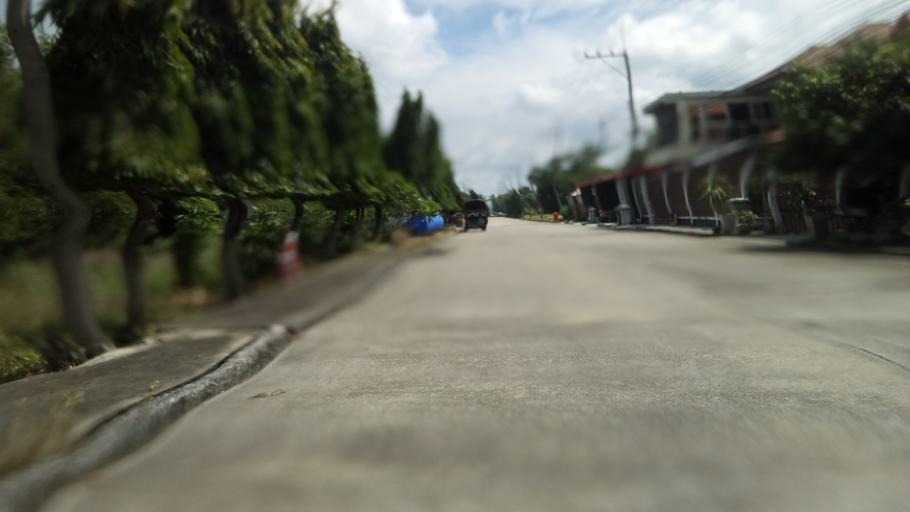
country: TH
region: Pathum Thani
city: Nong Suea
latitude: 14.0608
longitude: 100.8604
